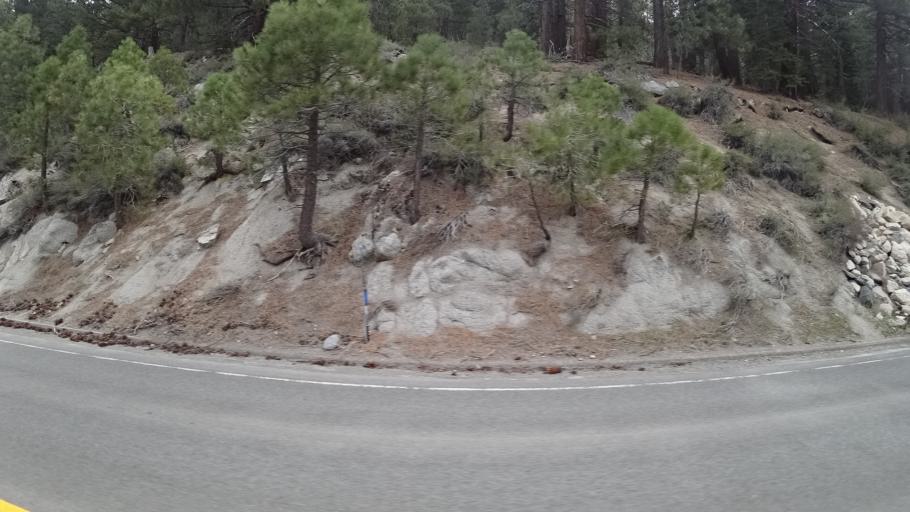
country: US
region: Nevada
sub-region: Washoe County
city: Incline Village
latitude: 39.1259
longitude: -119.9301
